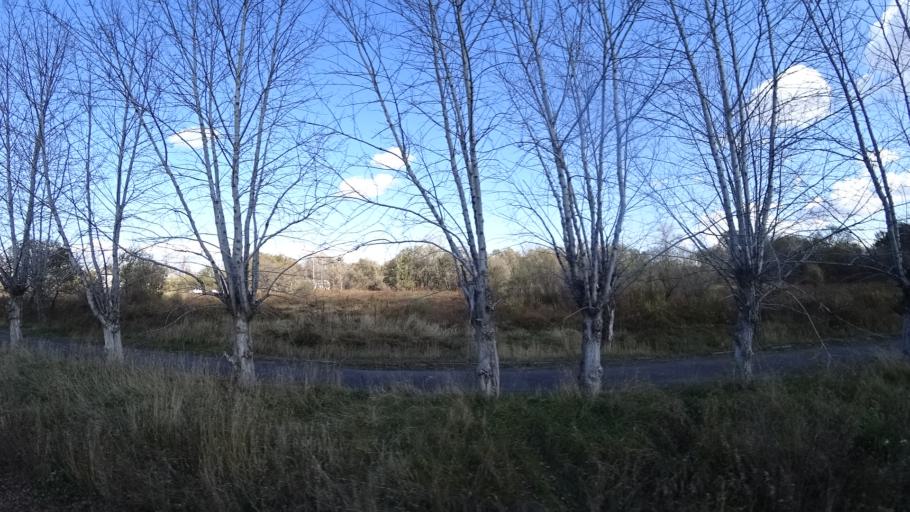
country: RU
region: Khabarovsk Krai
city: Amursk
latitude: 50.0964
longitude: 136.4965
